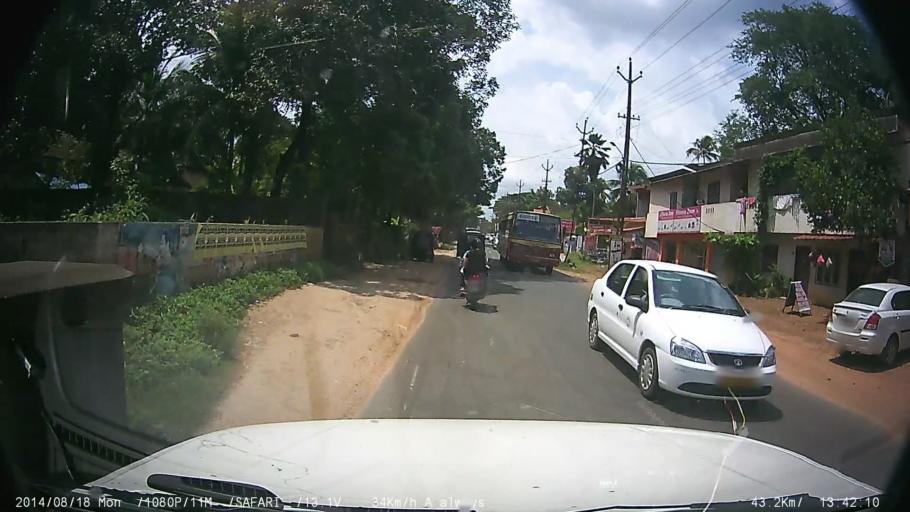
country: IN
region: Kerala
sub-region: Kottayam
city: Kottayam
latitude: 9.6762
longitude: 76.5581
